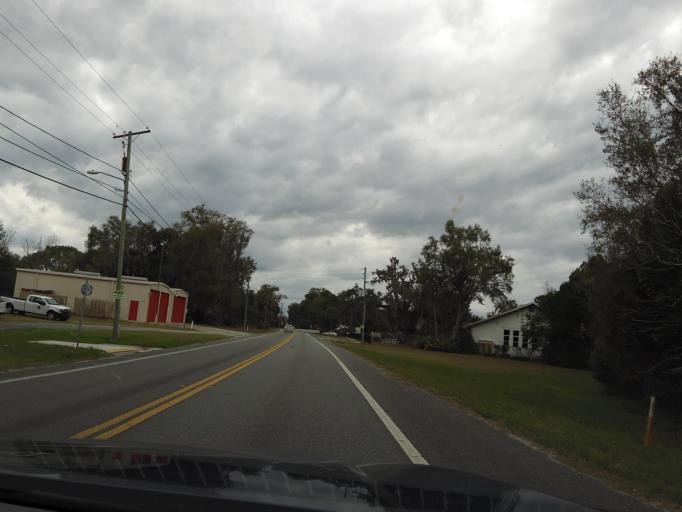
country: US
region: Florida
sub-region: Volusia County
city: Pierson
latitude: 29.3144
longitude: -81.4916
